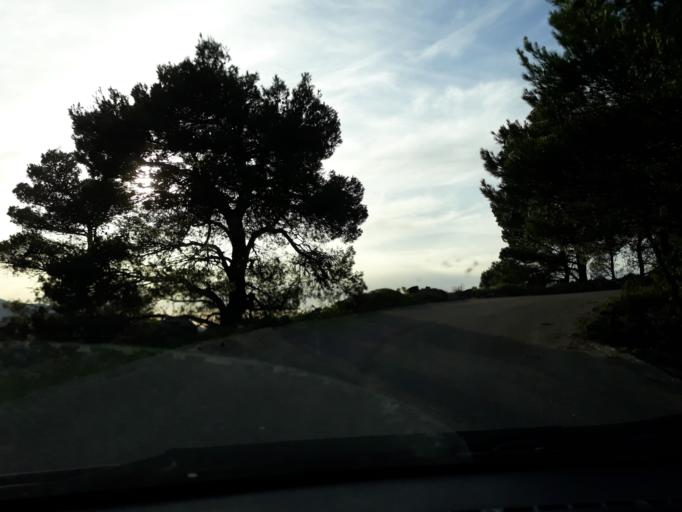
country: GR
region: Attica
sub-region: Nomarchia Anatolikis Attikis
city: Afidnes
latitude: 38.2140
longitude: 23.8088
